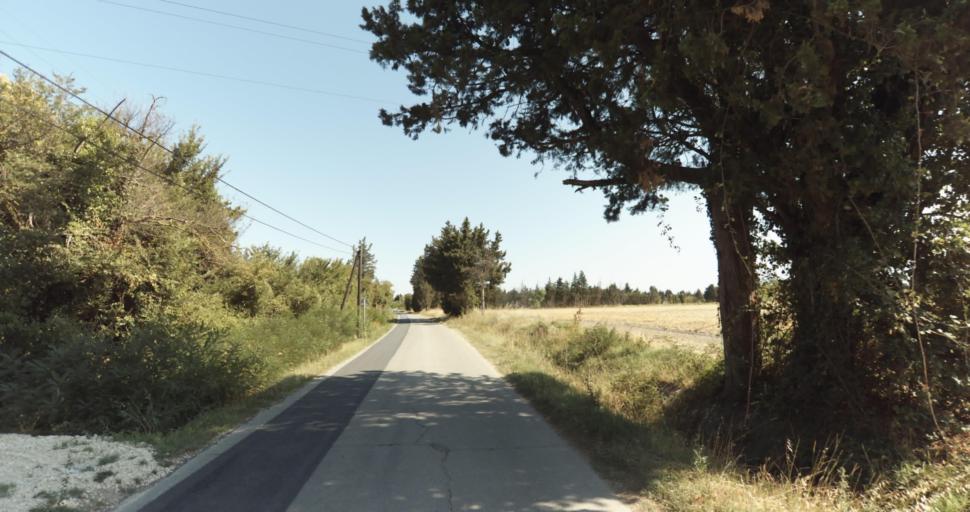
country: FR
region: Provence-Alpes-Cote d'Azur
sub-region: Departement du Vaucluse
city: Monteux
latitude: 44.0193
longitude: 4.9912
